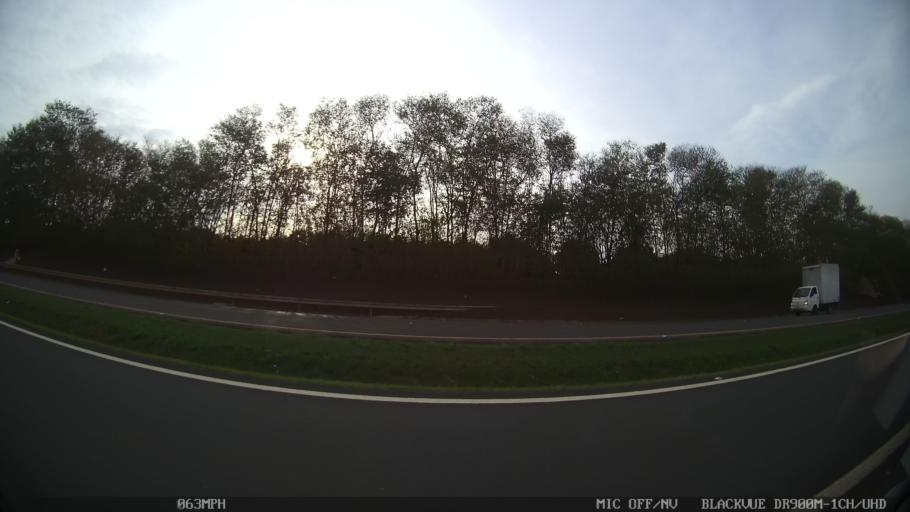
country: BR
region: Sao Paulo
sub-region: Iracemapolis
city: Iracemapolis
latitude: -22.6657
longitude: -47.5351
